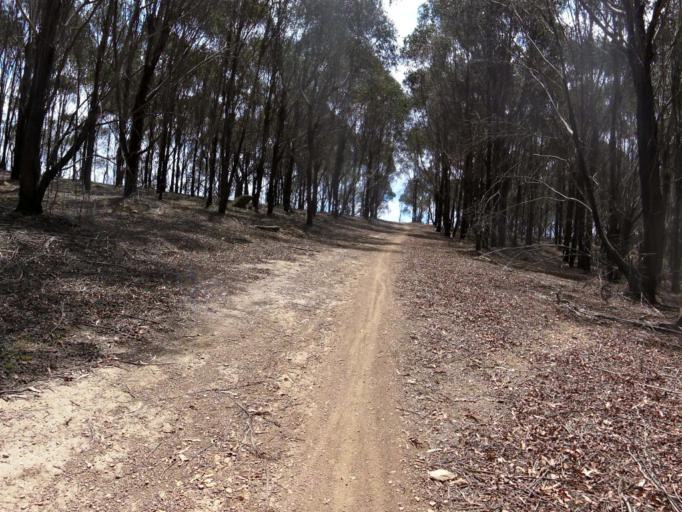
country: AU
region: Australian Capital Territory
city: Kaleen
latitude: -35.1268
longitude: 149.1233
